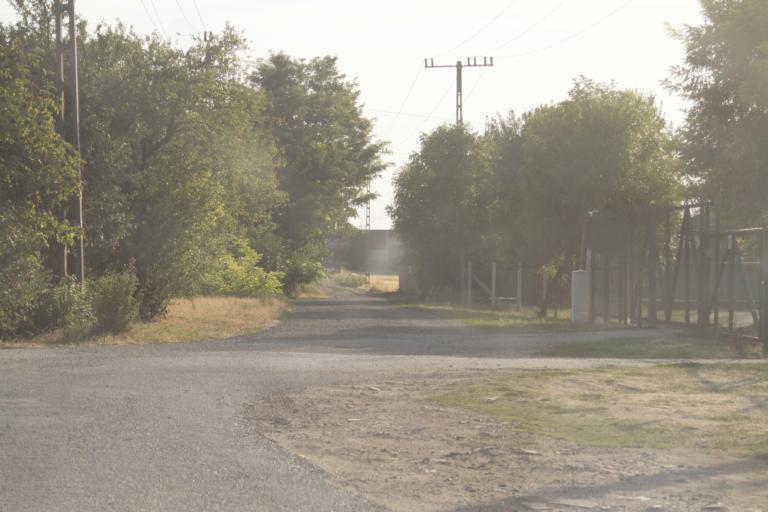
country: HU
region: Bekes
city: Bekescsaba
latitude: 46.6934
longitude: 21.0678
